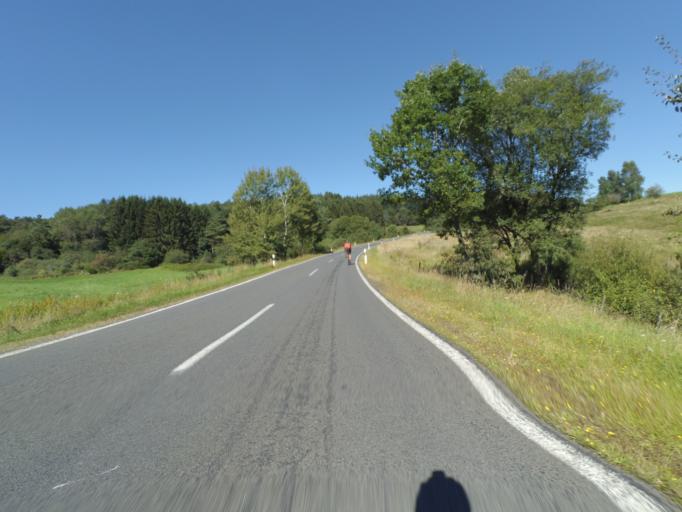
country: DE
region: Rheinland-Pfalz
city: Deudesfeld
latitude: 50.1083
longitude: 6.7331
